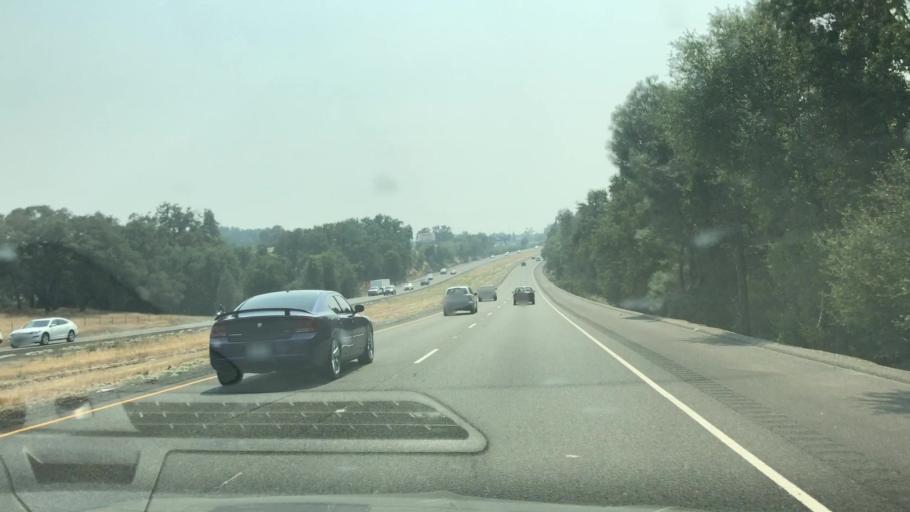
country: US
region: California
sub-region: El Dorado County
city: Shingle Springs
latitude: 38.6707
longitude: -120.9250
